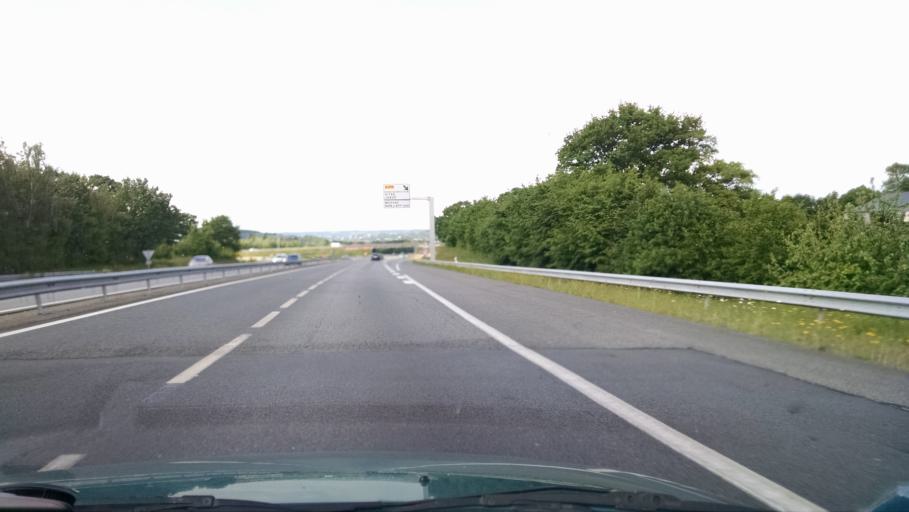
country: FR
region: Brittany
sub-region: Departement d'Ille-et-Vilaine
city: Bain-de-Bretagne
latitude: 47.8470
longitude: -1.6960
